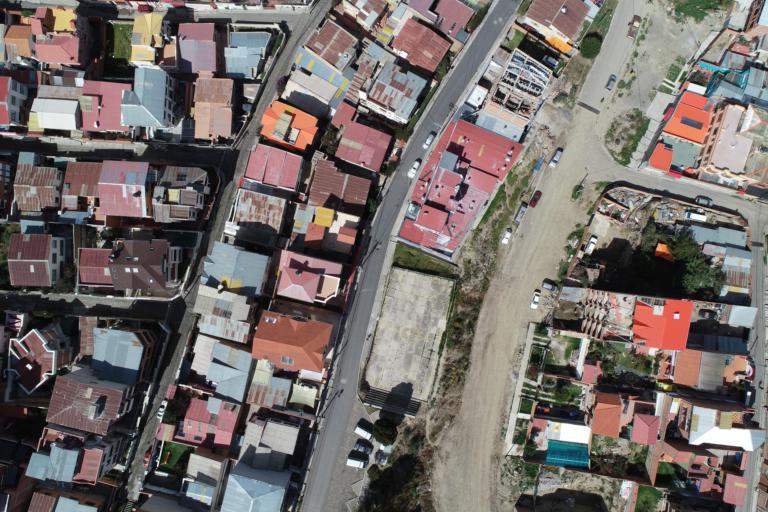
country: BO
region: La Paz
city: La Paz
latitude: -16.5191
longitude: -68.1036
